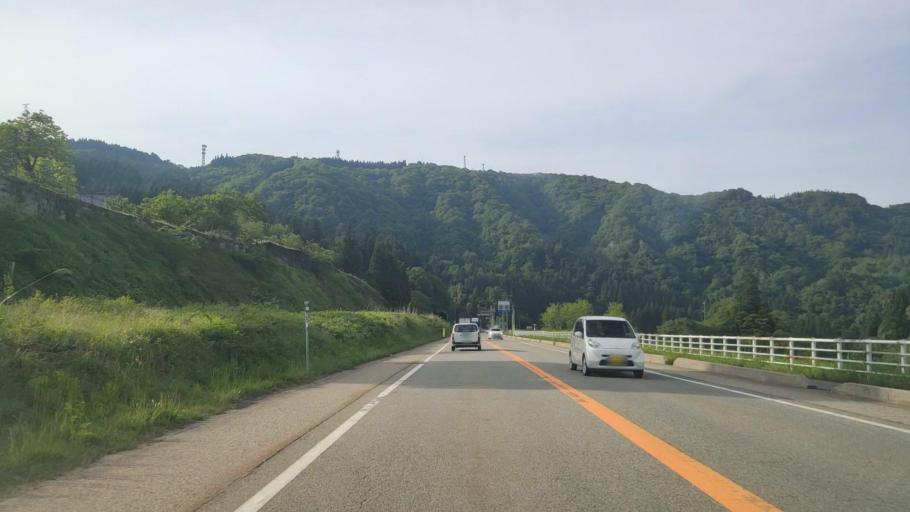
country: JP
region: Toyama
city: Yatsuomachi-higashikumisaka
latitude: 36.4909
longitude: 137.2369
